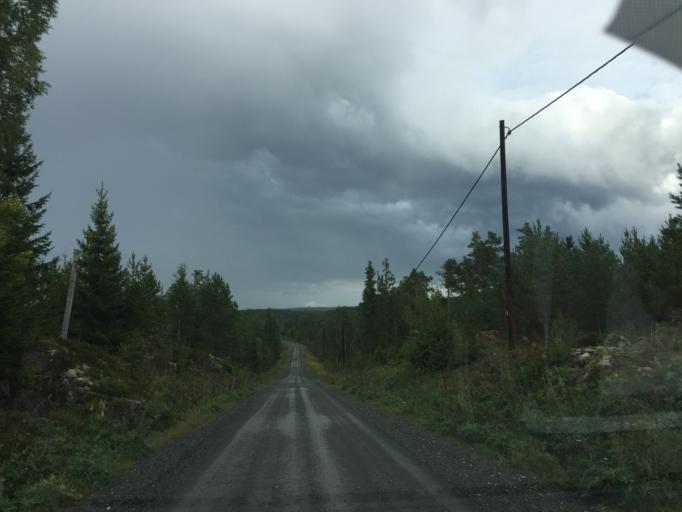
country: SE
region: Vaermland
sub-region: Filipstads Kommun
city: Lesjofors
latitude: 59.9158
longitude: 14.1196
